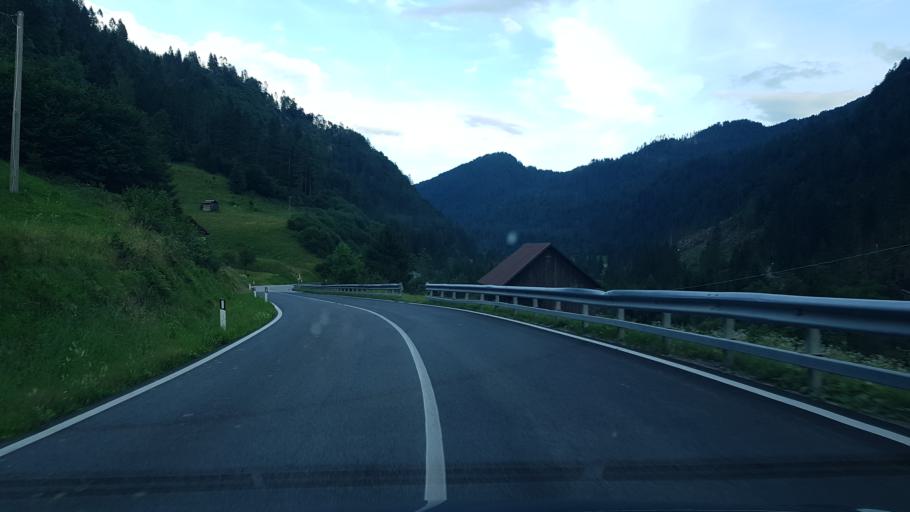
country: IT
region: Friuli Venezia Giulia
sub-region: Provincia di Udine
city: Forni Avoltri
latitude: 46.5816
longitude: 12.7840
